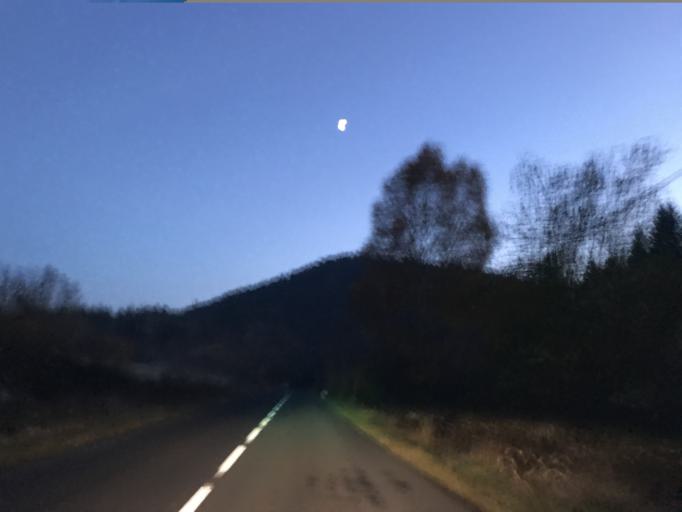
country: FR
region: Rhone-Alpes
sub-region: Departement de la Loire
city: Noiretable
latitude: 45.7703
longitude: 3.6819
